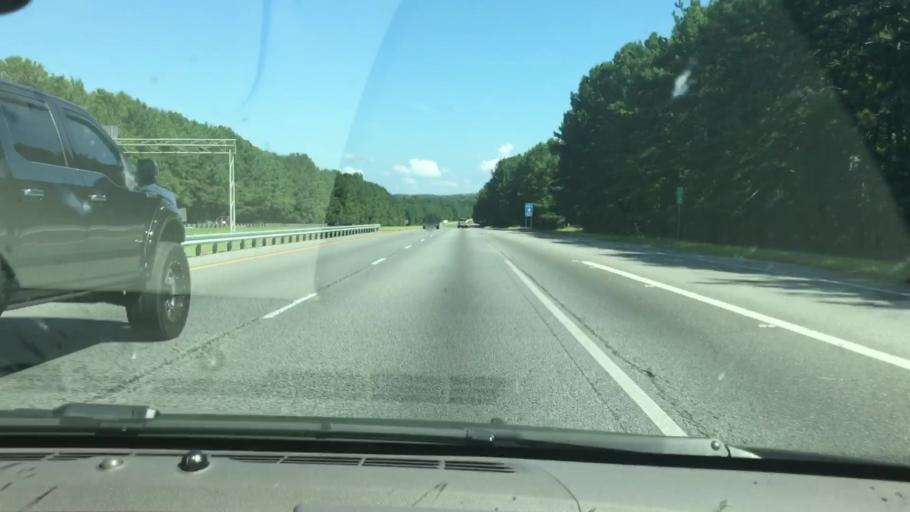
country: US
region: Alabama
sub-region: Russell County
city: Phenix City
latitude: 32.5717
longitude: -84.9617
